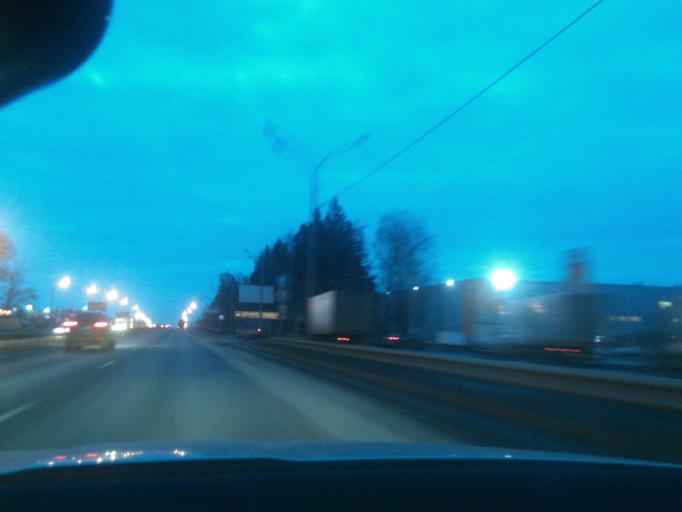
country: RU
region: Moskovskaya
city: Skhodnya
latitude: 55.9800
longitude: 37.2950
